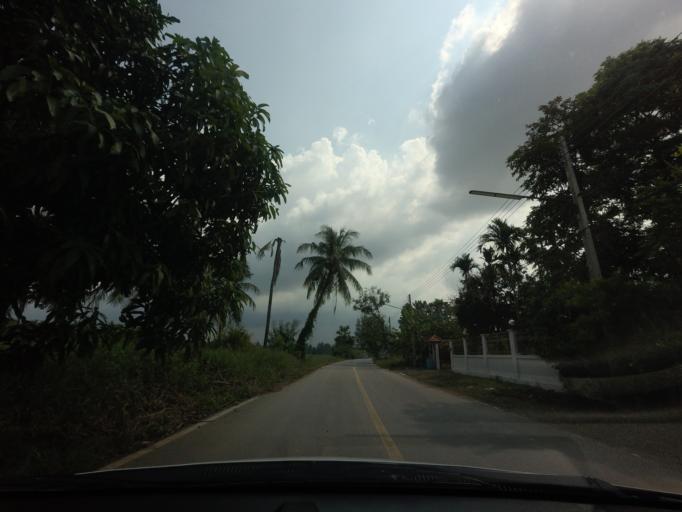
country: TH
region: Nakhon Pathom
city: Nakhon Chai Si
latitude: 13.8009
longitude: 100.2209
